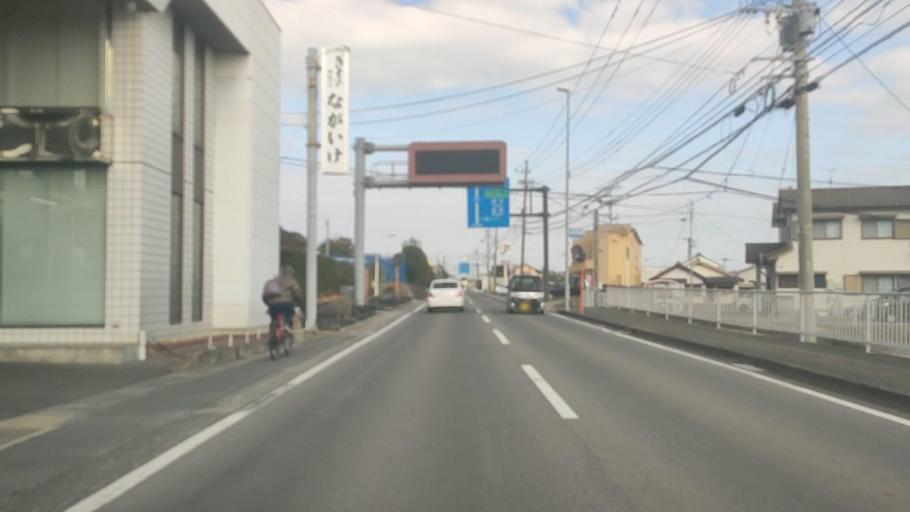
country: JP
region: Nagasaki
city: Shimabara
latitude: 32.7192
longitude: 130.3532
